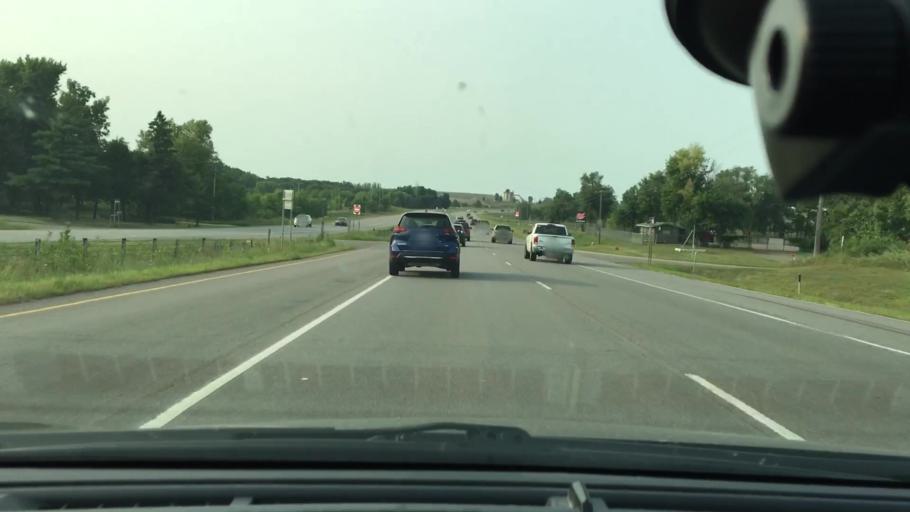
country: US
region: Minnesota
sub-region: Sherburne County
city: Elk River
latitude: 45.3618
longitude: -93.5633
